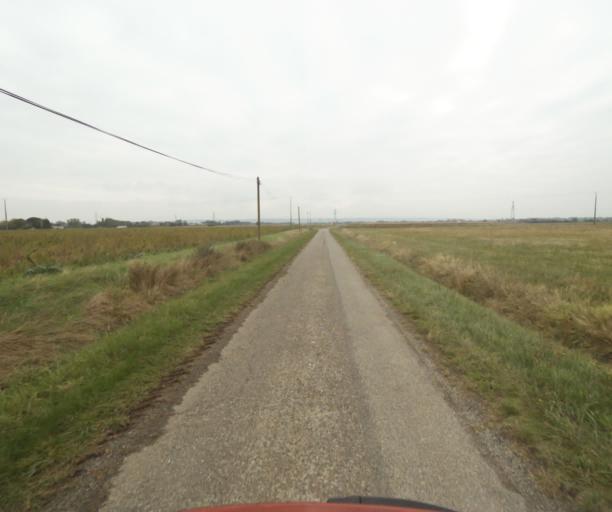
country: FR
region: Midi-Pyrenees
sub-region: Departement du Tarn-et-Garonne
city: Verdun-sur-Garonne
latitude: 43.7982
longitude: 1.2343
